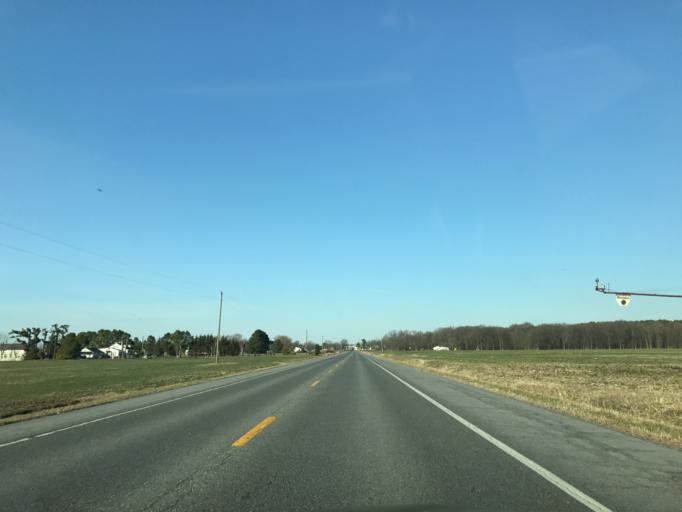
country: US
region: Maryland
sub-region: Caroline County
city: Greensboro
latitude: 39.1290
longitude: -75.8660
